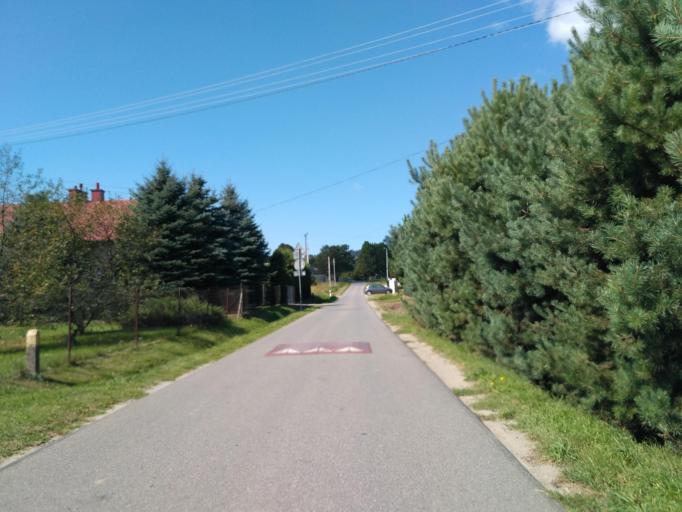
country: PL
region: Subcarpathian Voivodeship
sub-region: Powiat jasielski
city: Brzyska
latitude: 49.8043
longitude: 21.4084
